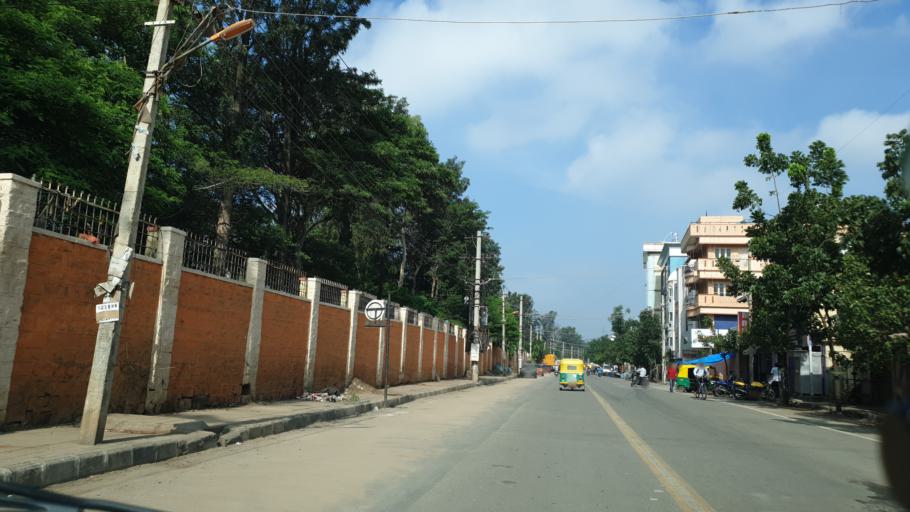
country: IN
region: Karnataka
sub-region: Bangalore Urban
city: Bangalore
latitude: 12.9731
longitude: 77.6763
